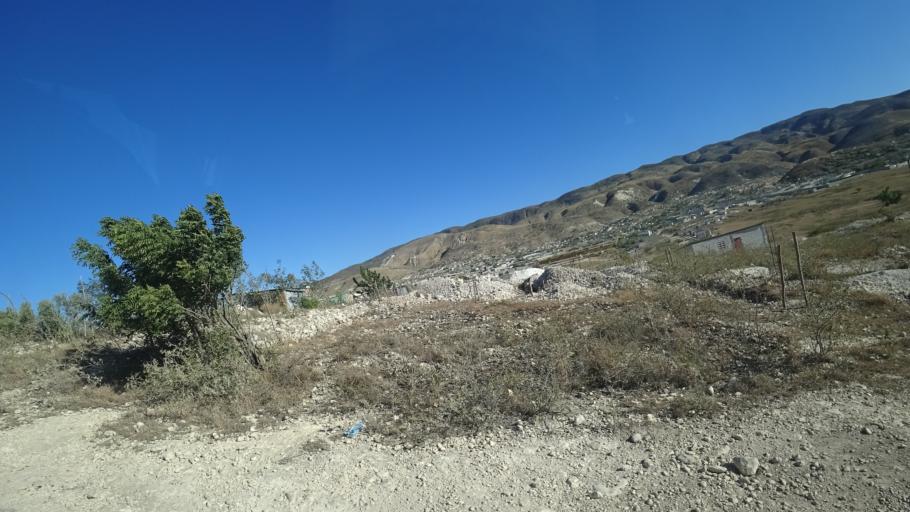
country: HT
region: Ouest
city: Cabaret
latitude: 18.6837
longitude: -72.3188
